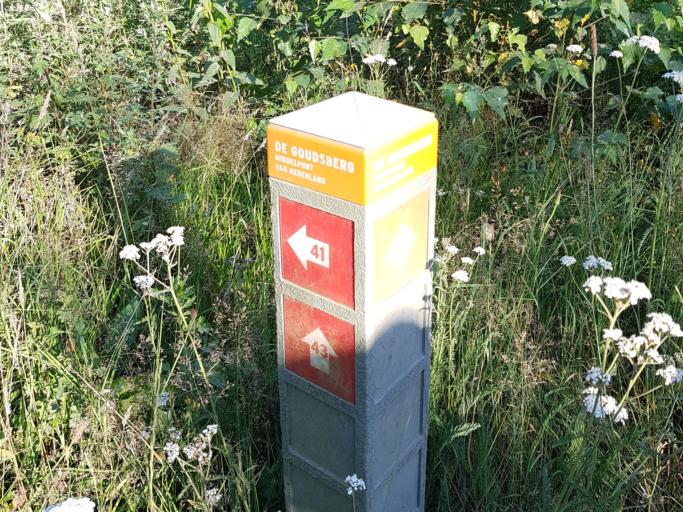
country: NL
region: Gelderland
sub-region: Gemeente Ede
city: Wekerom
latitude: 52.0942
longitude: 5.6972
